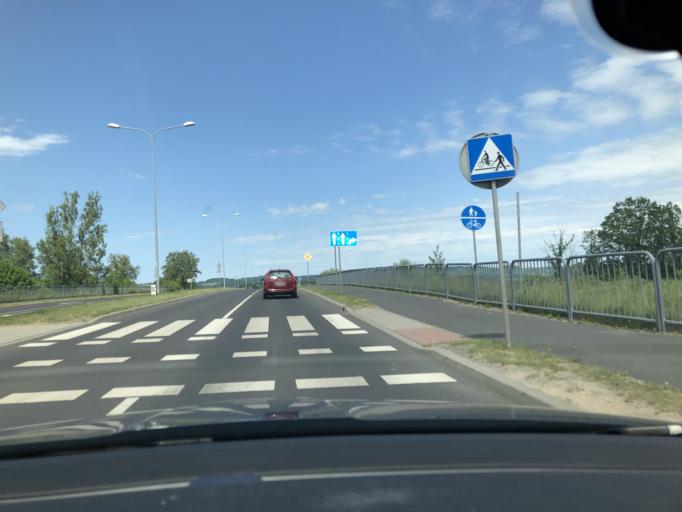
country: PL
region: Lower Silesian Voivodeship
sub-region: Jelenia Gora
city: Jelenia Gora
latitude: 50.8980
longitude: 15.7714
